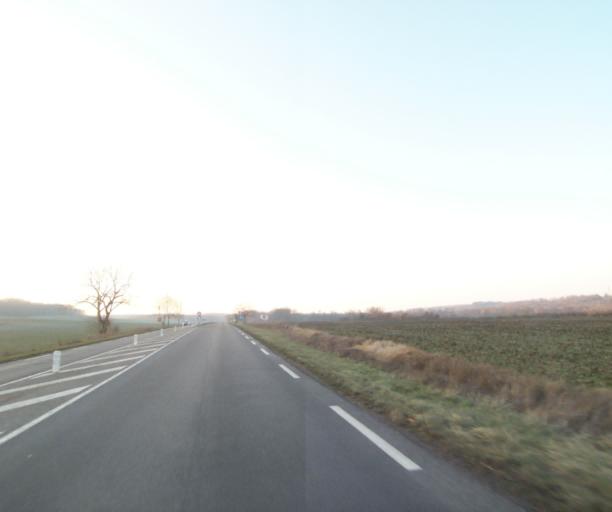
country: FR
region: Lorraine
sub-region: Departement de la Meuse
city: Ancerville
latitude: 48.6066
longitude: 5.0221
